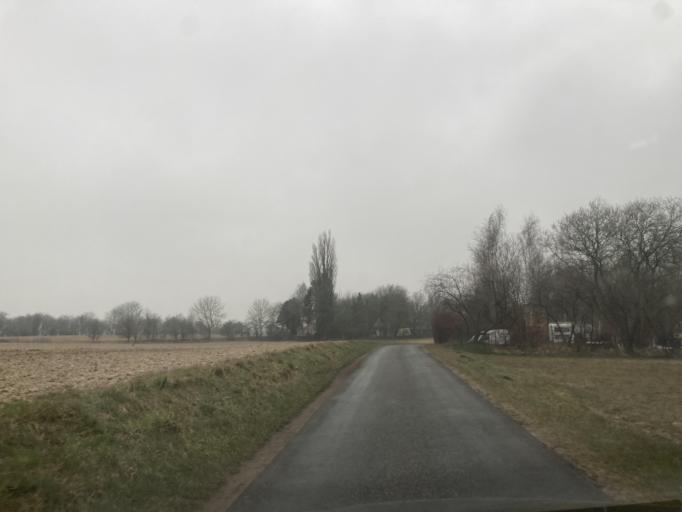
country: DK
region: Zealand
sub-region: Vordingborg Kommune
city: Neder Vindinge
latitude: 55.1592
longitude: 11.8972
